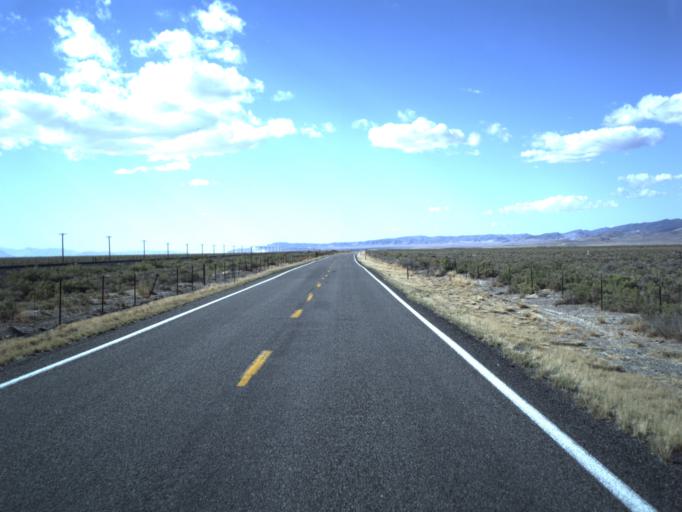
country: US
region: Utah
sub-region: Millard County
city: Delta
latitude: 39.1367
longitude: -112.7276
